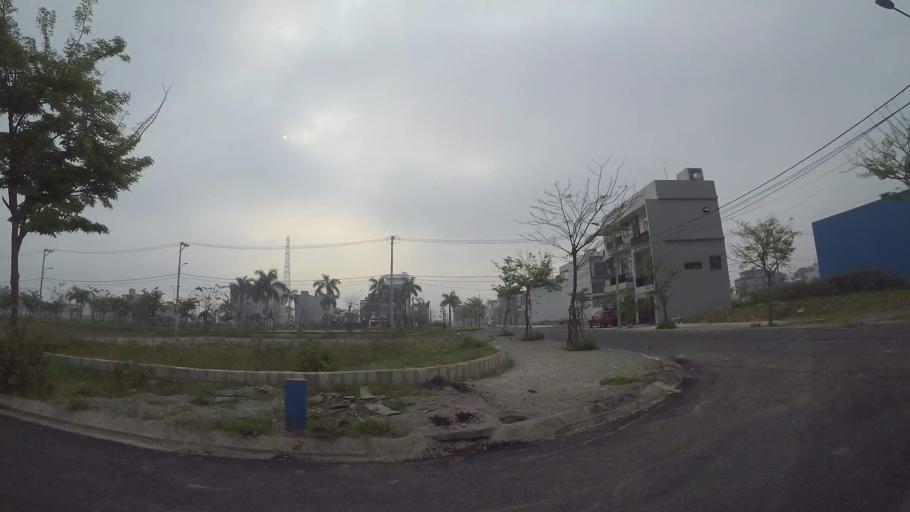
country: VN
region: Da Nang
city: Ngu Hanh Son
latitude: 16.0204
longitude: 108.2334
